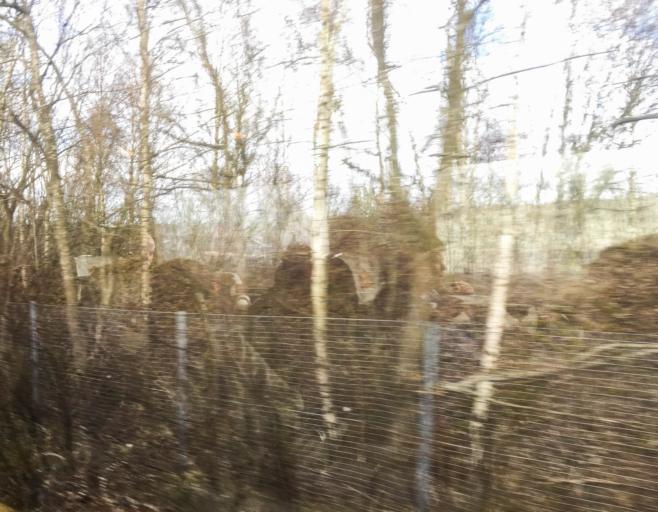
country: GB
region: Scotland
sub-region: North Lanarkshire
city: Newarthill
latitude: 55.7842
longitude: -3.9472
